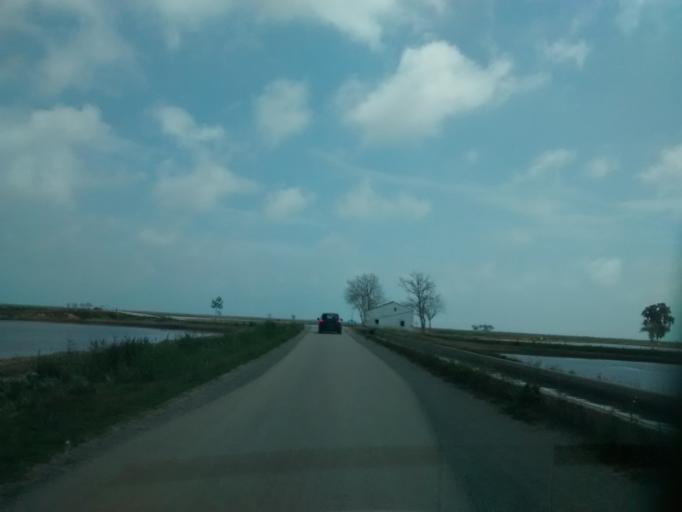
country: ES
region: Catalonia
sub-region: Provincia de Tarragona
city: Deltebre
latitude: 40.6832
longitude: 0.7935
